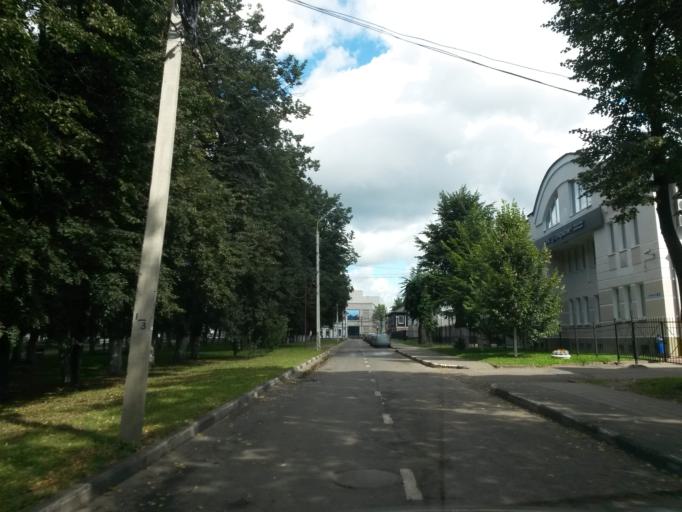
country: RU
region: Jaroslavl
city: Yaroslavl
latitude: 57.6241
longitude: 39.8718
